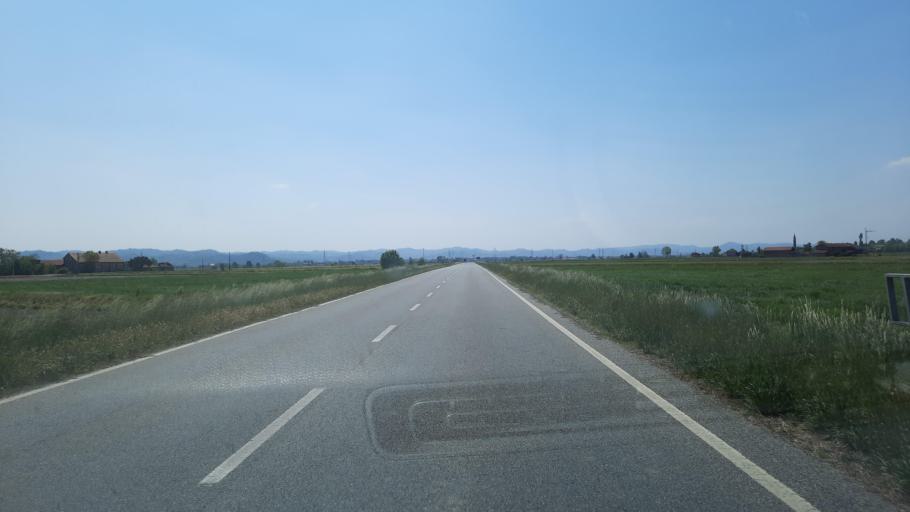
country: IT
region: Piedmont
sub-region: Provincia di Vercelli
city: Lamporo
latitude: 45.2167
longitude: 8.1353
